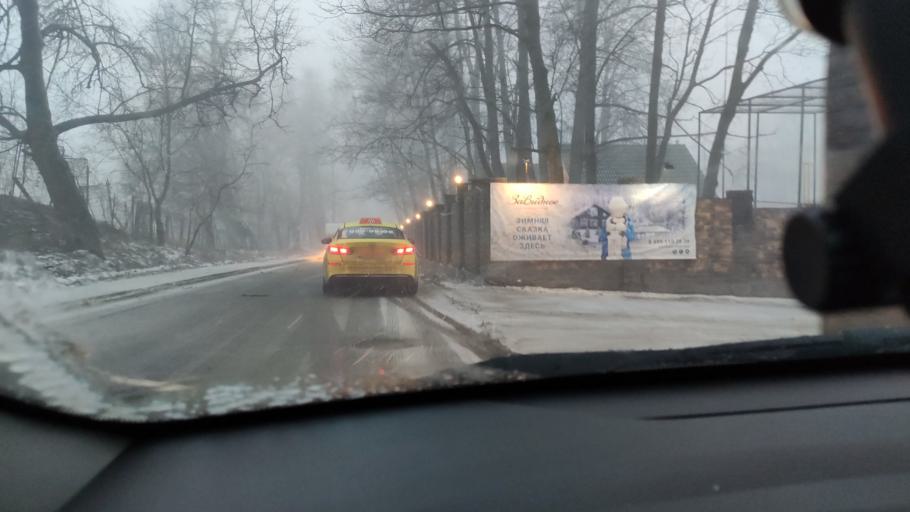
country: RU
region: Moskovskaya
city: Biryulevo Zapadnoye
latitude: 55.5618
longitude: 37.6408
